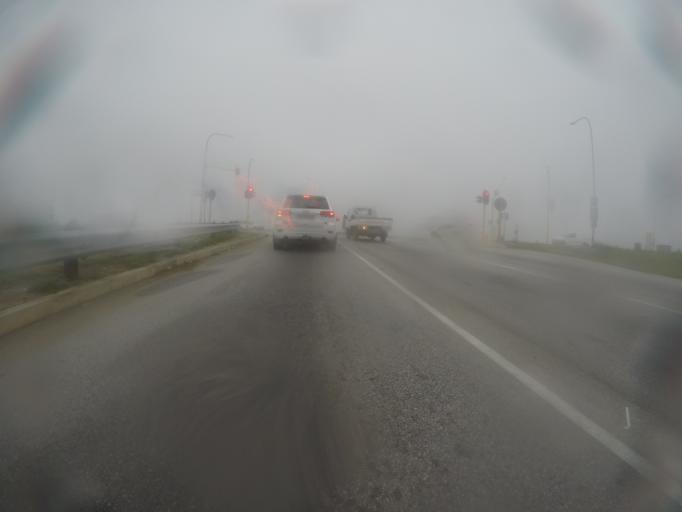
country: ZA
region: Western Cape
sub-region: Eden District Municipality
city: George
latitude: -33.9975
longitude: 22.4447
